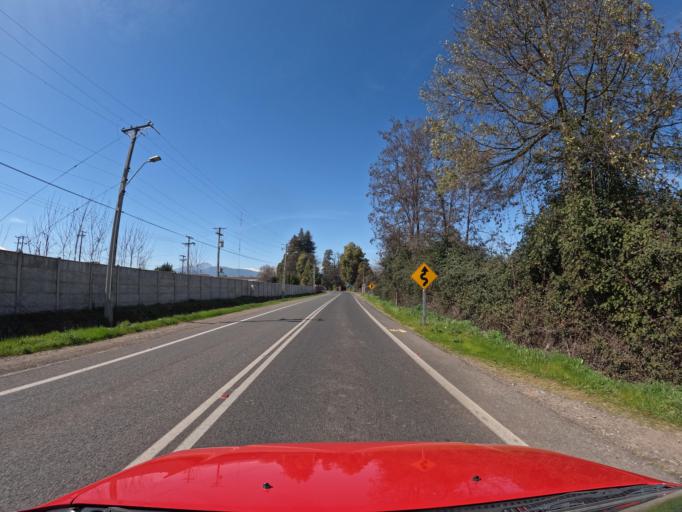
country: CL
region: Maule
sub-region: Provincia de Curico
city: Teno
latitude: -34.9691
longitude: -71.0183
